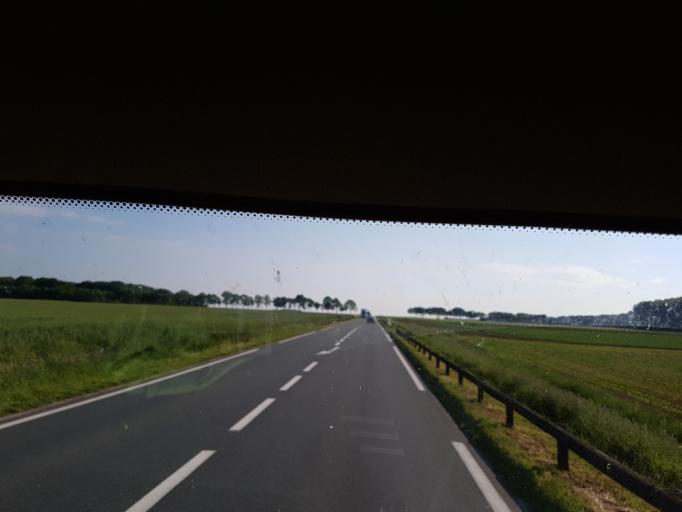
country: FR
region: Picardie
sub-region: Departement de la Somme
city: Crecy-en-Ponthieu
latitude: 50.2114
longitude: 1.9083
